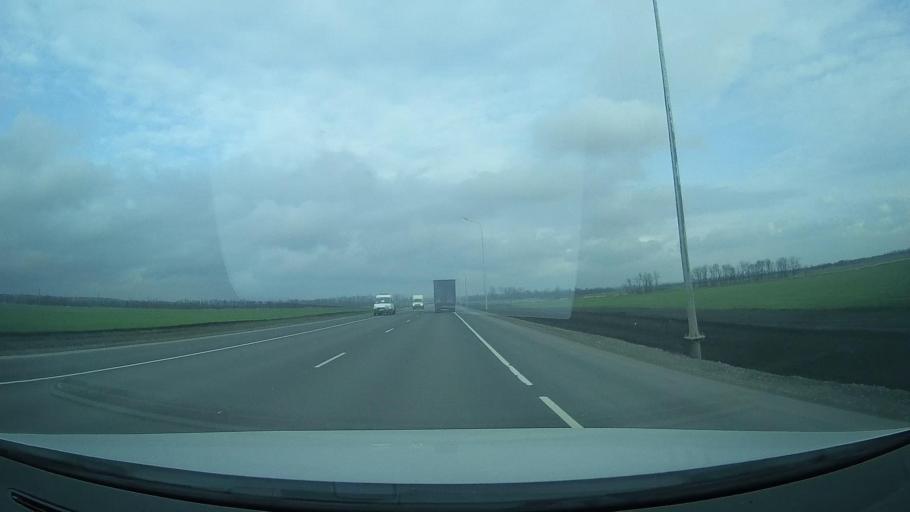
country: RU
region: Rostov
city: Grushevskaya
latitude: 47.4416
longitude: 39.8746
